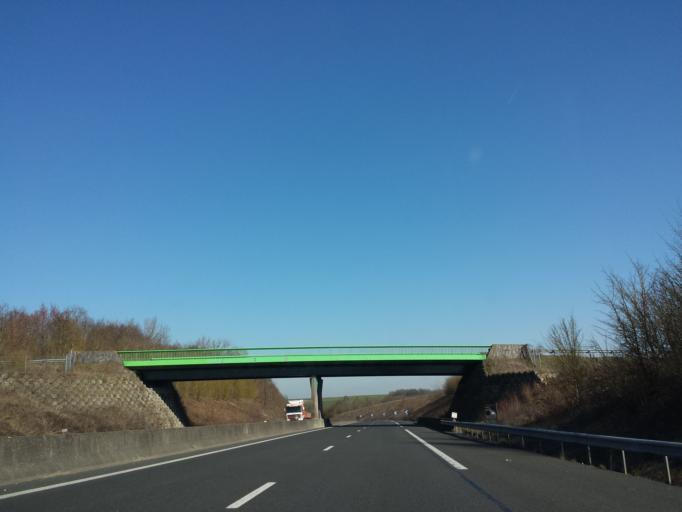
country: FR
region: Picardie
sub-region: Departement de l'Oise
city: Breteuil
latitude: 49.5743
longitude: 2.2017
